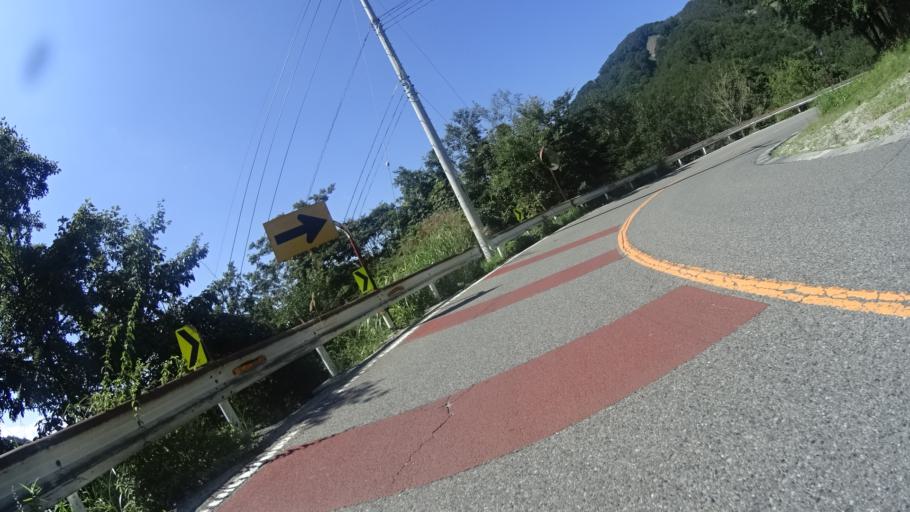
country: JP
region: Yamanashi
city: Enzan
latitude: 35.7713
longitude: 138.8049
